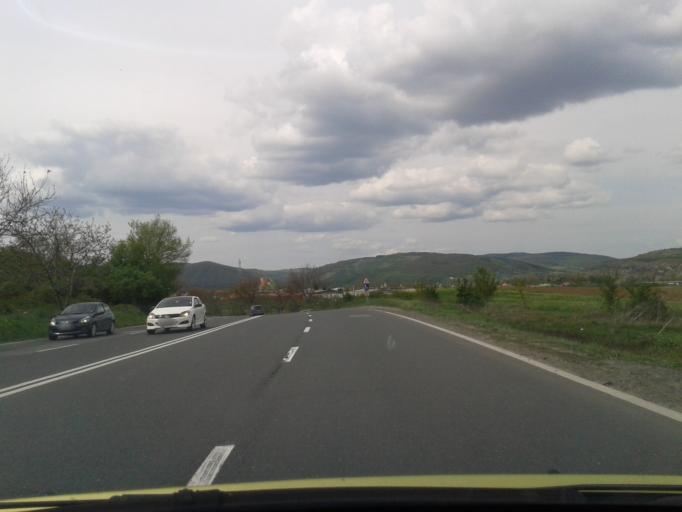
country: RO
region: Hunedoara
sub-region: Comuna Soimus
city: Soimus
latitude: 45.9080
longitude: 22.8681
